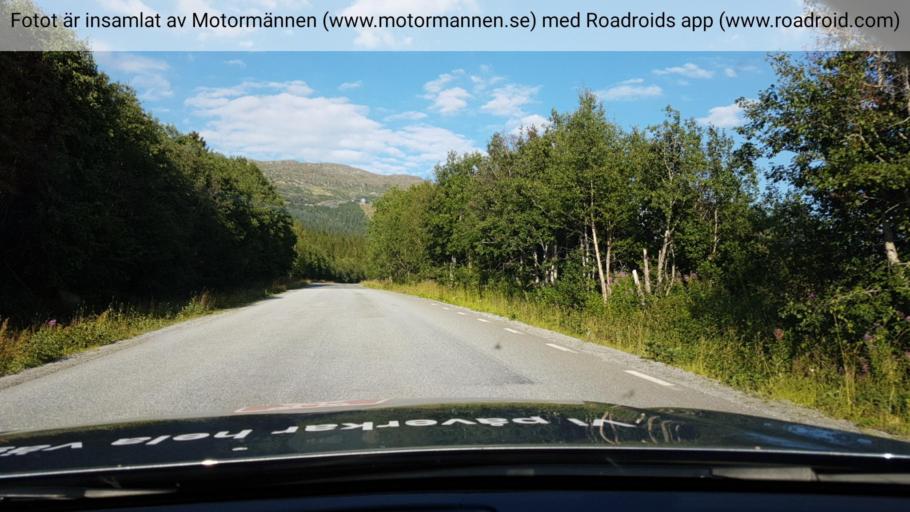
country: SE
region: Jaemtland
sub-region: Are Kommun
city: Are
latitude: 63.4081
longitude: 13.0279
